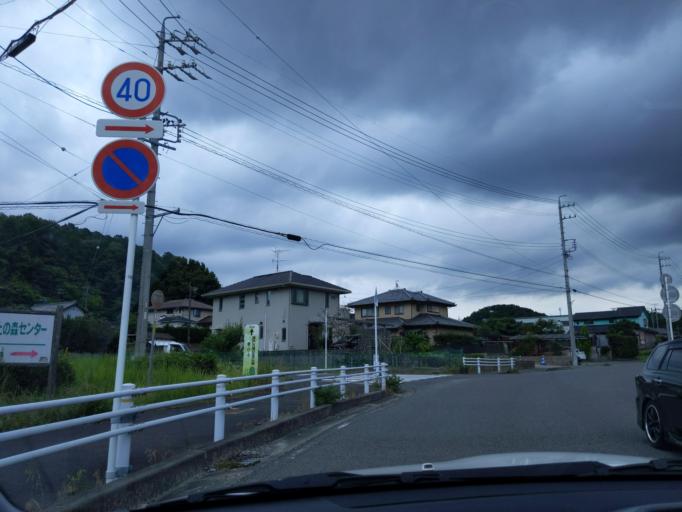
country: JP
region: Aichi
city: Seto
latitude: 35.1939
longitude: 137.1082
